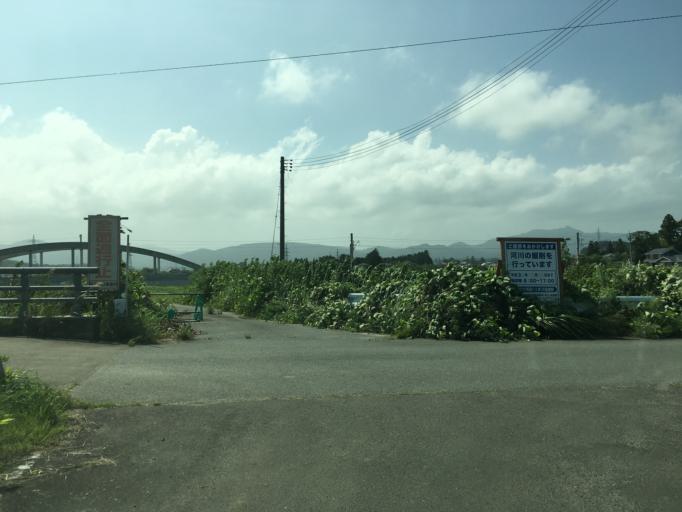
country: JP
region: Miyagi
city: Marumori
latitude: 37.8315
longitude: 140.9266
